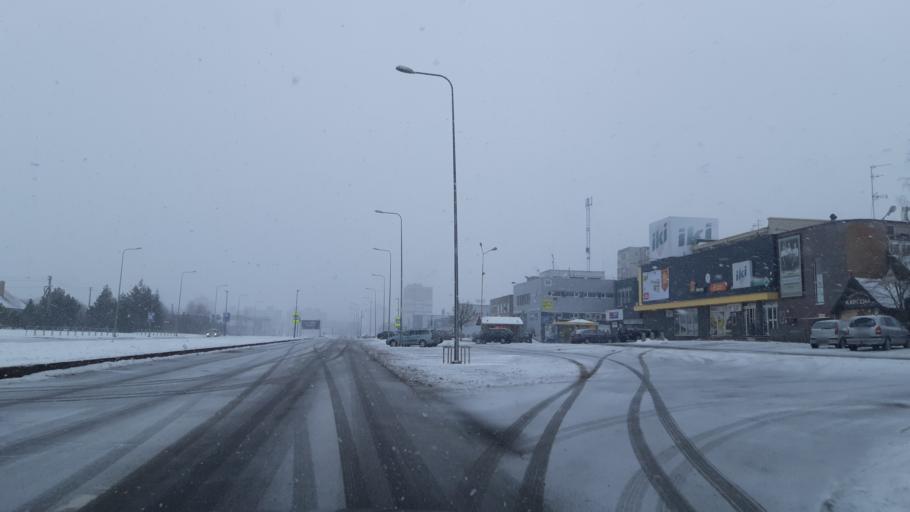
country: LT
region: Kauno apskritis
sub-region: Kaunas
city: Silainiai
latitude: 54.9270
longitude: 23.8776
